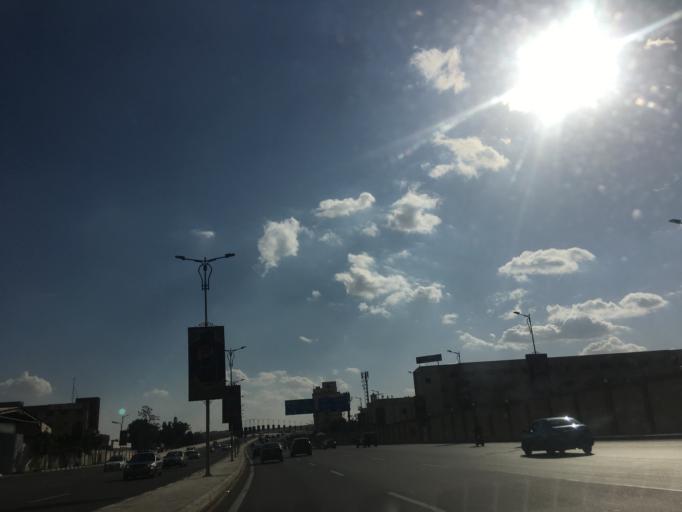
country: EG
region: Muhafazat al Qahirah
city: Cairo
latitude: 30.0475
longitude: 31.3073
